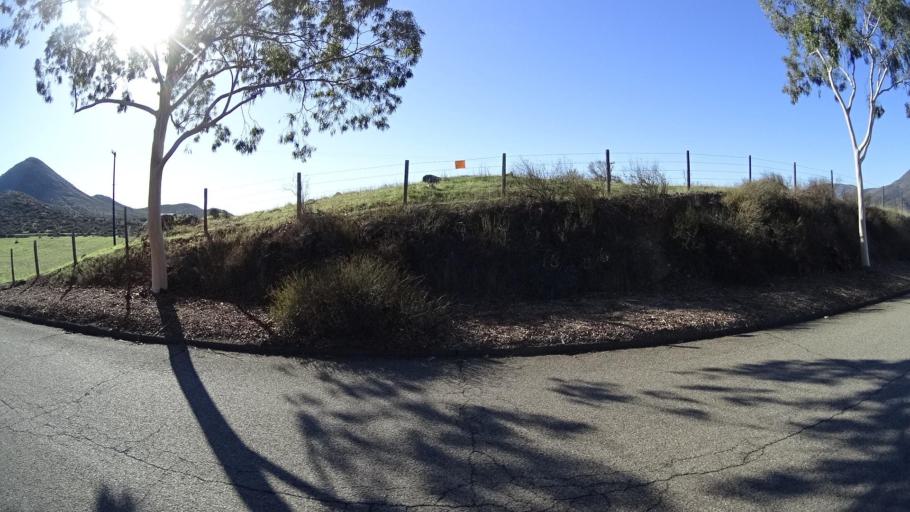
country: US
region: California
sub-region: San Diego County
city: Jamul
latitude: 32.6973
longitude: -116.8548
